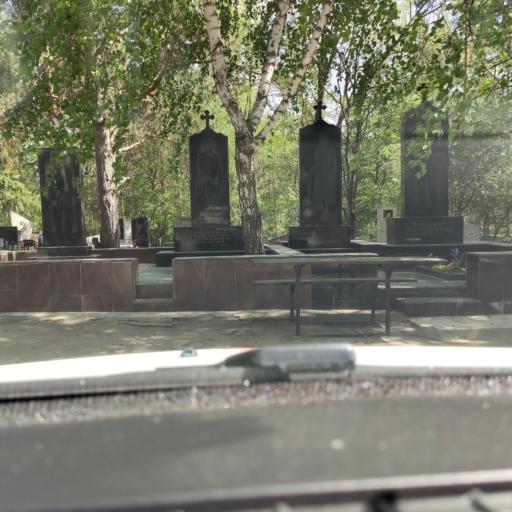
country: RU
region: Samara
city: Samara
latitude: 53.1147
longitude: 50.2340
